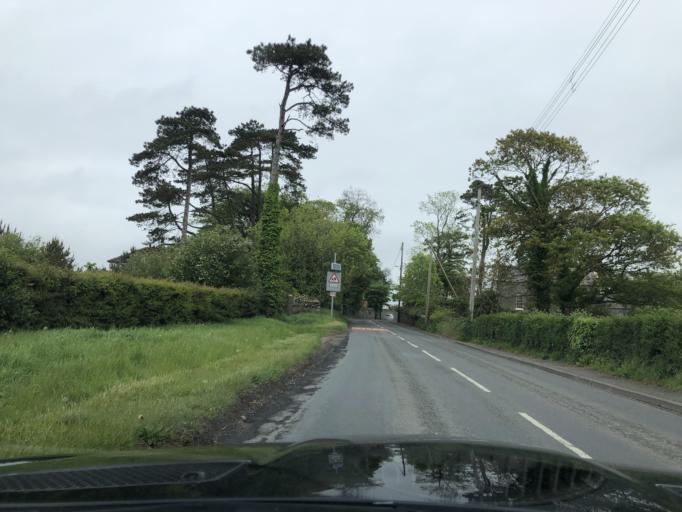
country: GB
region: Northern Ireland
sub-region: Down District
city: Portaferry
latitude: 54.3674
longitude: -5.5600
